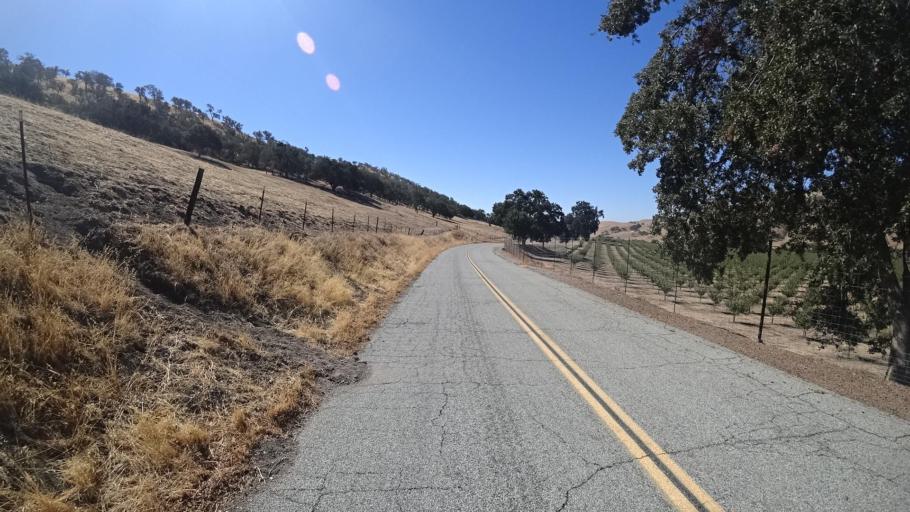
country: US
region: California
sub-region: San Luis Obispo County
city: San Miguel
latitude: 35.8064
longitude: -120.6746
